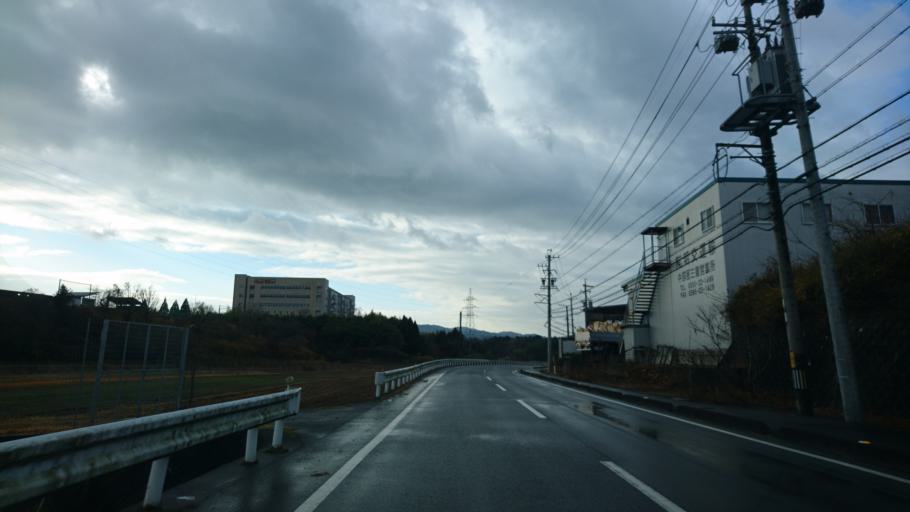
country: JP
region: Mie
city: Ueno-ebisumachi
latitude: 34.7222
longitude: 136.0802
